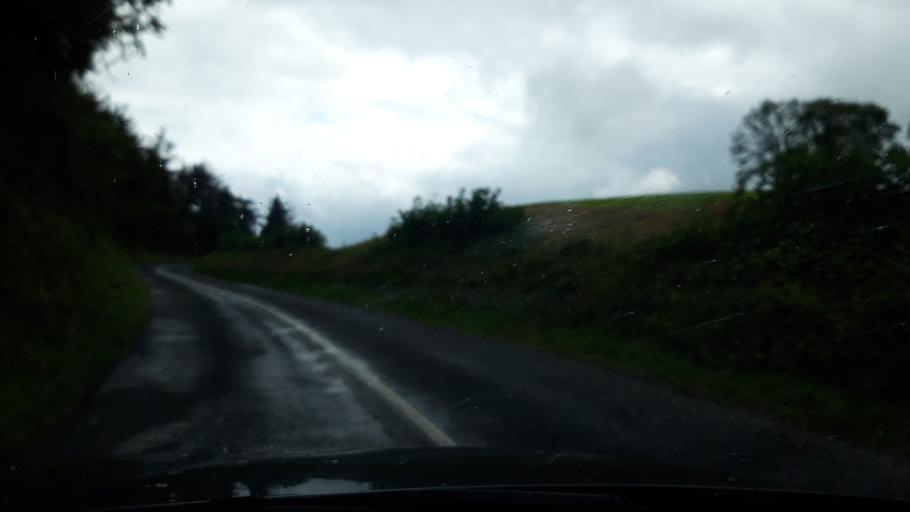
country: IE
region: Munster
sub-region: County Cork
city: Castlemartyr
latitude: 52.1383
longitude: -8.0463
